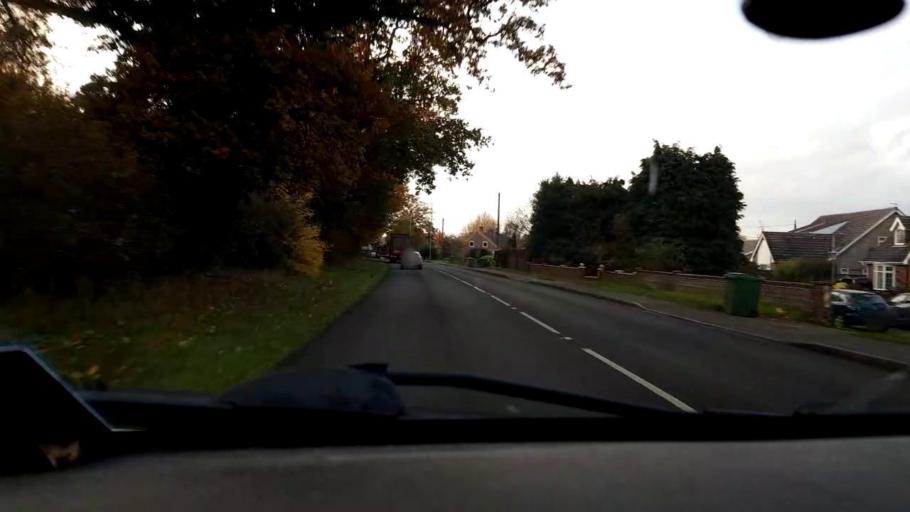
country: GB
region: England
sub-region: Norfolk
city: Mattishall
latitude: 52.7201
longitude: 1.1188
